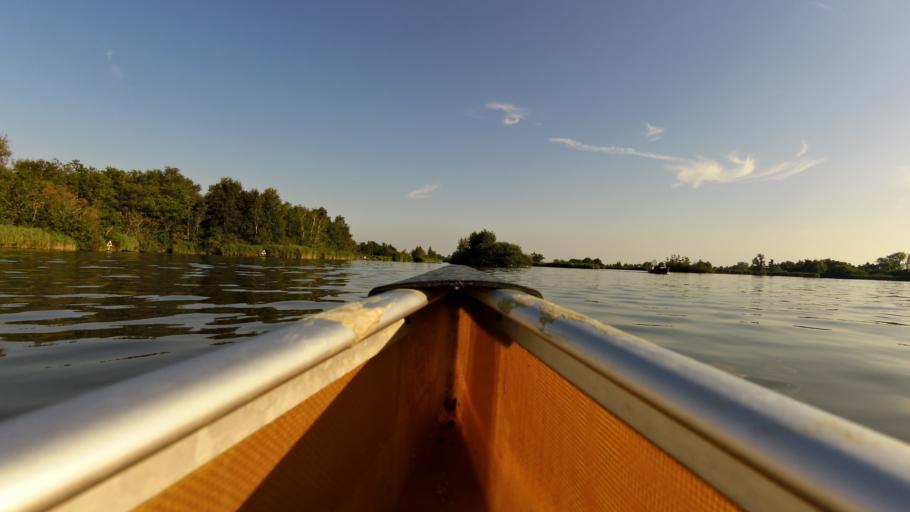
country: NL
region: South Holland
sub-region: Gemeente Nieuwkoop
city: Nieuwkoop
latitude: 52.1380
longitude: 4.7737
